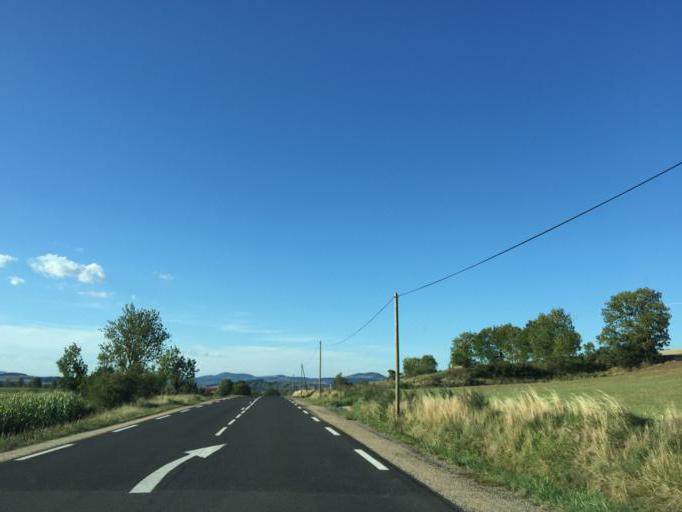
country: FR
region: Auvergne
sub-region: Departement de la Haute-Loire
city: Espaly-Saint-Marcel
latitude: 45.0265
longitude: 3.8446
